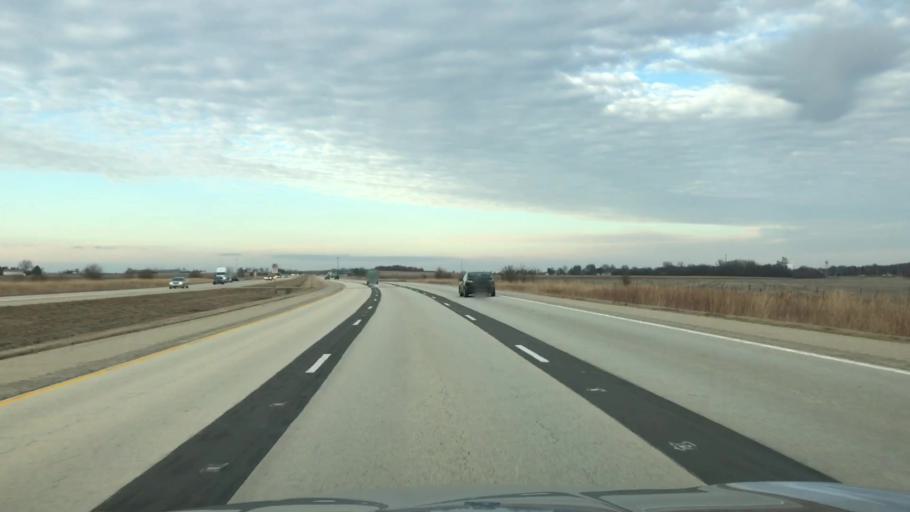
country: US
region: Illinois
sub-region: Sangamon County
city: Williamsville
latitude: 40.0056
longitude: -89.5011
